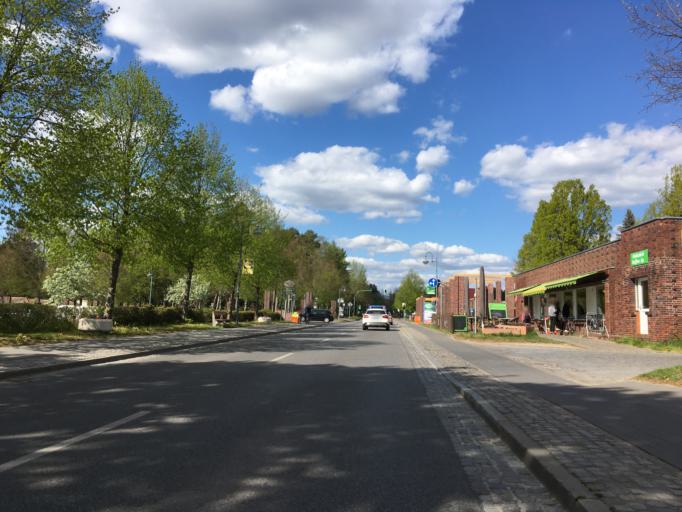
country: DE
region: Brandenburg
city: Wandlitz
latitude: 52.7553
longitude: 13.4727
